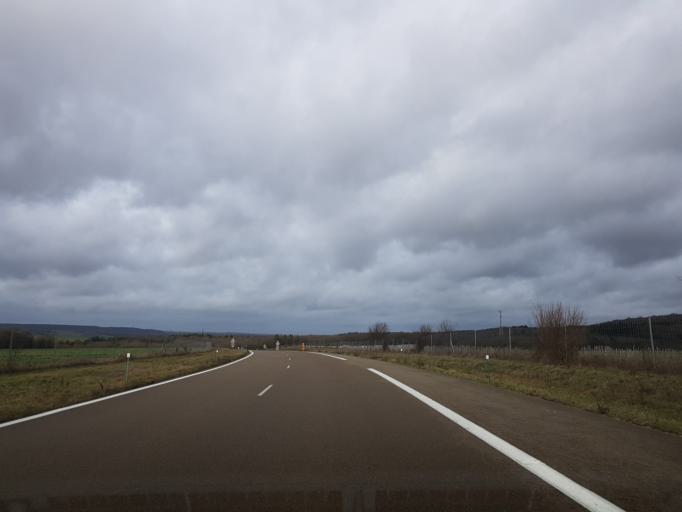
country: FR
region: Champagne-Ardenne
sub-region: Departement de la Haute-Marne
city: Rolampont
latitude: 47.9125
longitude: 5.2281
